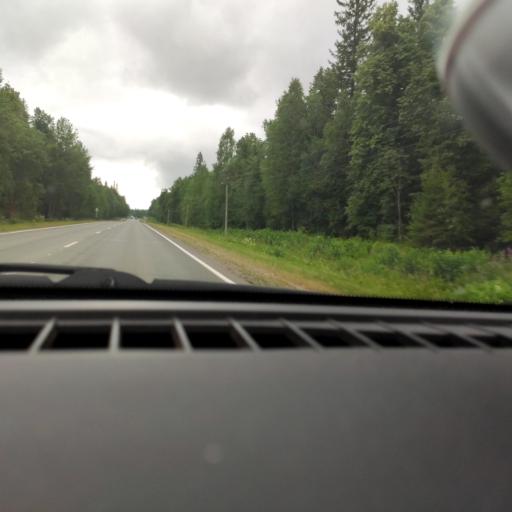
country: RU
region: Perm
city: Polazna
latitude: 58.3039
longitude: 56.1564
